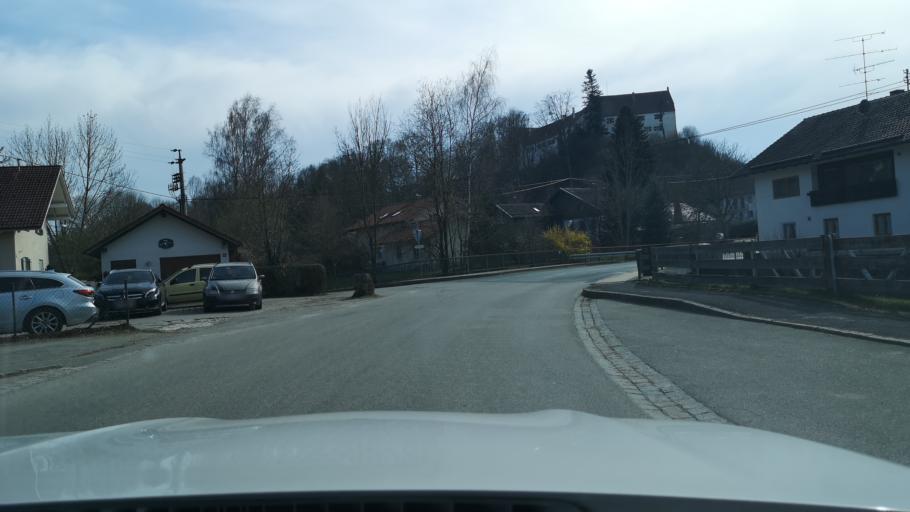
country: DE
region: Bavaria
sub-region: Upper Bavaria
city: Isen
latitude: 48.1902
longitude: 12.0500
